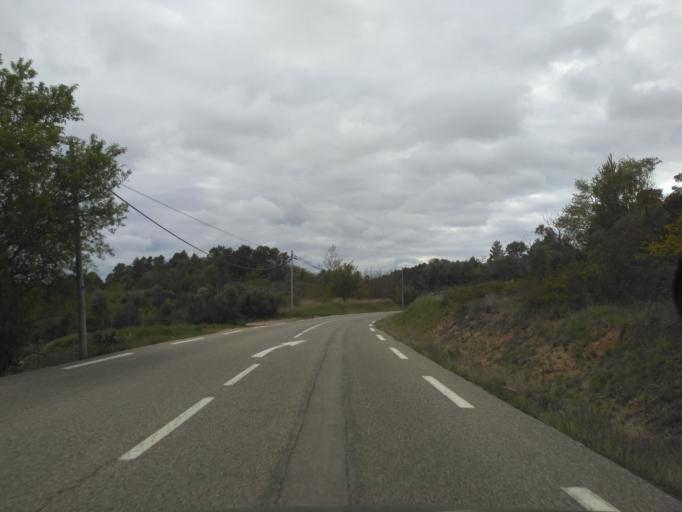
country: FR
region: Provence-Alpes-Cote d'Azur
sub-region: Departement du Var
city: Barjols
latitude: 43.6063
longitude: 5.9529
